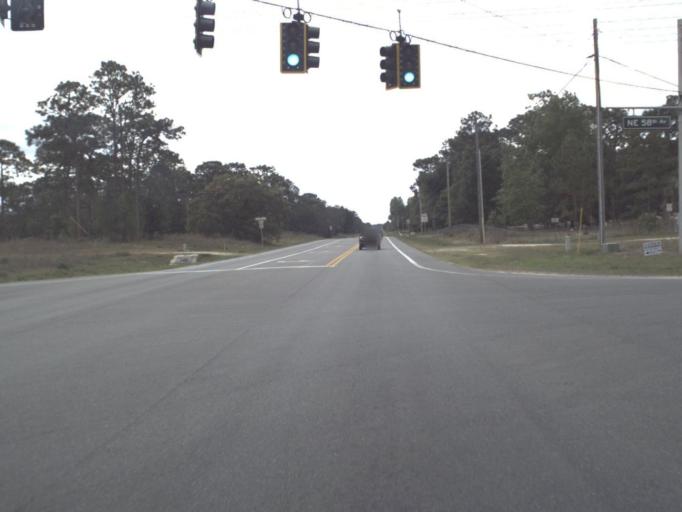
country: US
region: Florida
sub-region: Marion County
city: Ocala
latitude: 29.2416
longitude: -82.0541
